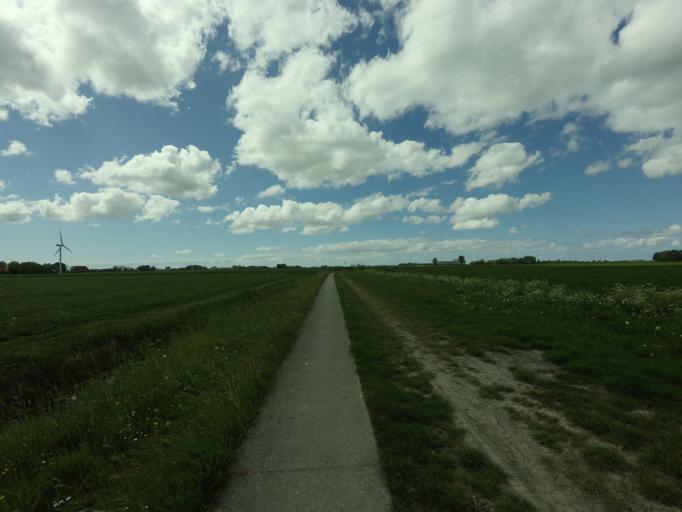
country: NL
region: Friesland
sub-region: Gemeente Franekeradeel
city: Tzum
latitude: 53.1288
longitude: 5.5632
